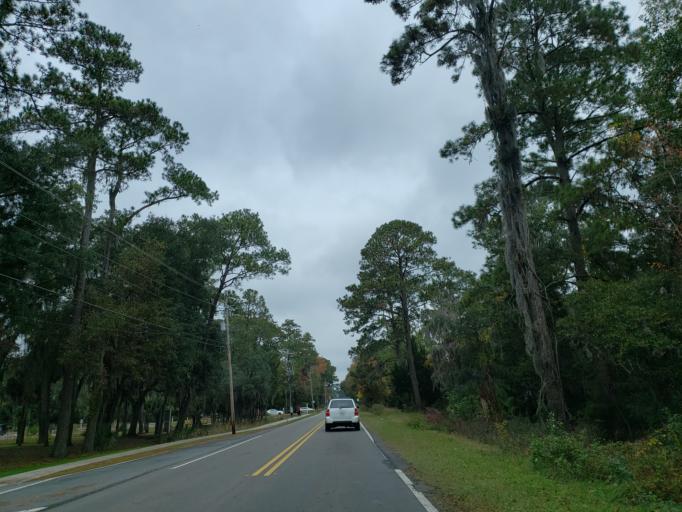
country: US
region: Georgia
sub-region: Chatham County
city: Wilmington Island
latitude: 32.0119
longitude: -80.9740
